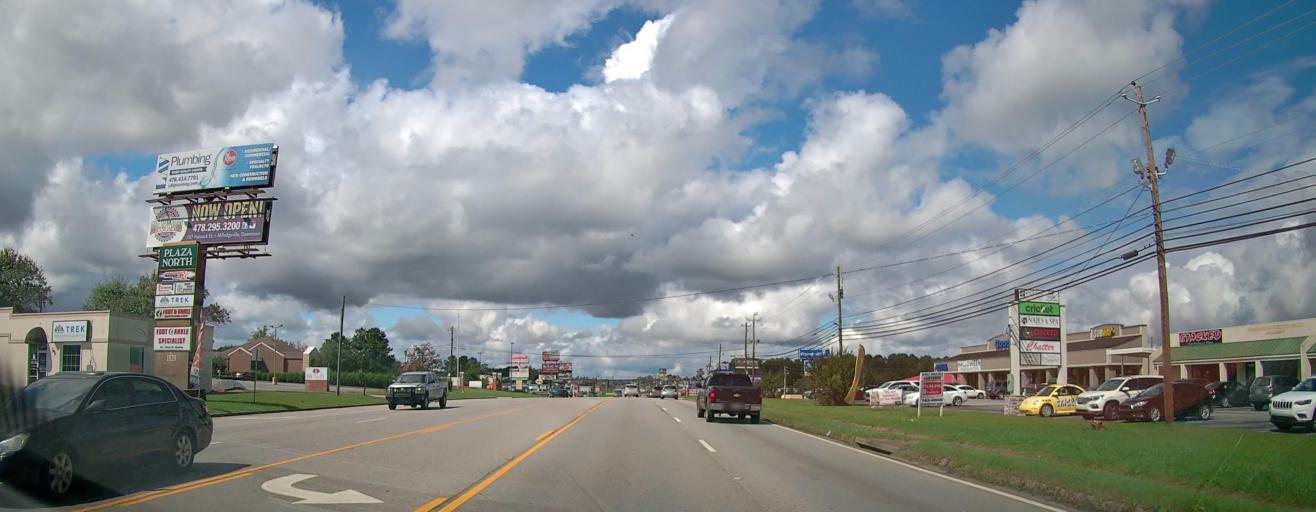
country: US
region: Georgia
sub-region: Baldwin County
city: Milledgeville
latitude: 33.1024
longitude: -83.2490
